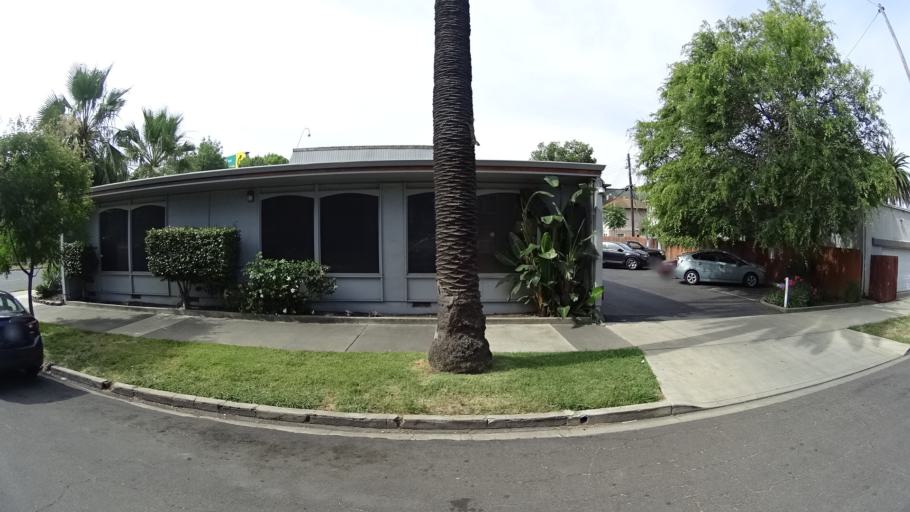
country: US
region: California
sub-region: Sacramento County
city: Sacramento
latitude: 38.5616
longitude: -121.4739
